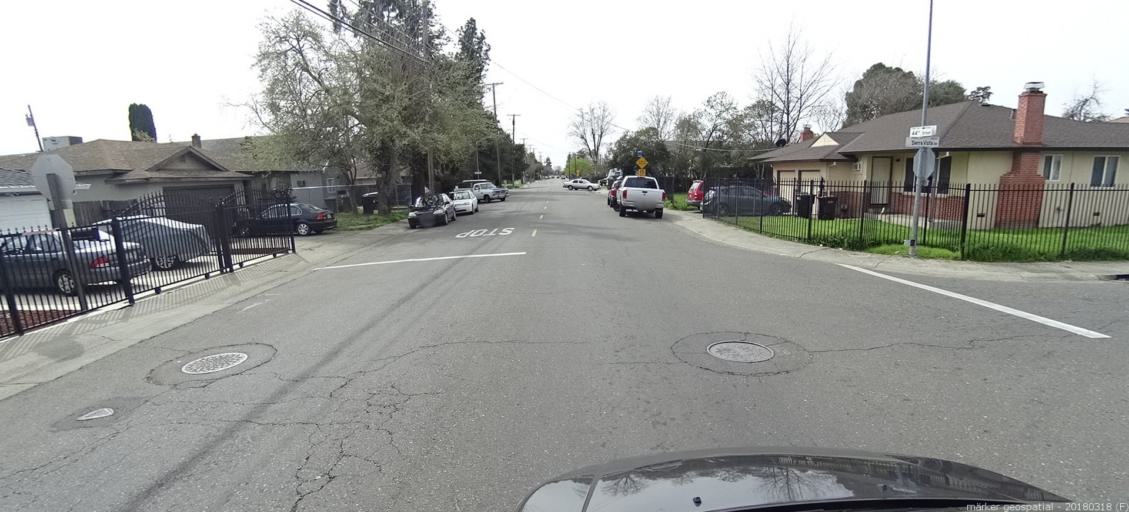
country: US
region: California
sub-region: Sacramento County
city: Parkway
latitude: 38.5303
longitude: -121.4563
